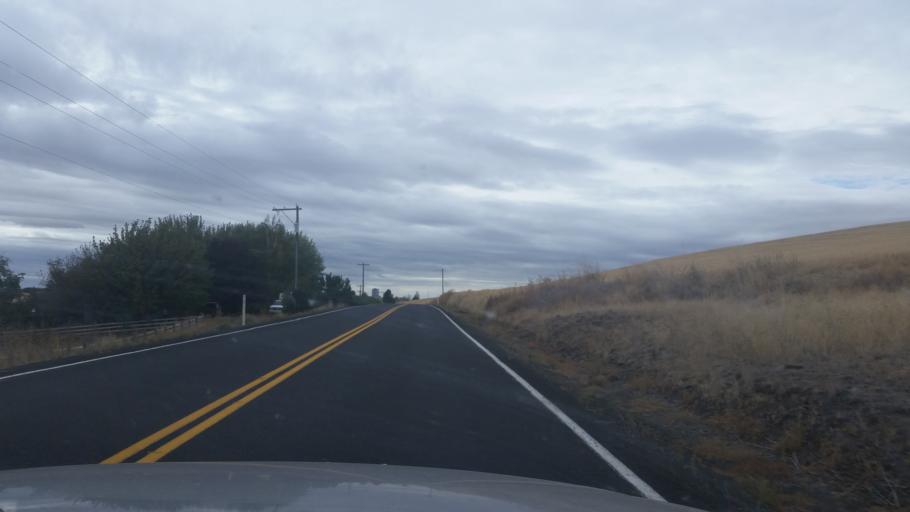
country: US
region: Washington
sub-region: Lincoln County
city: Davenport
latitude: 47.5132
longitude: -117.9419
